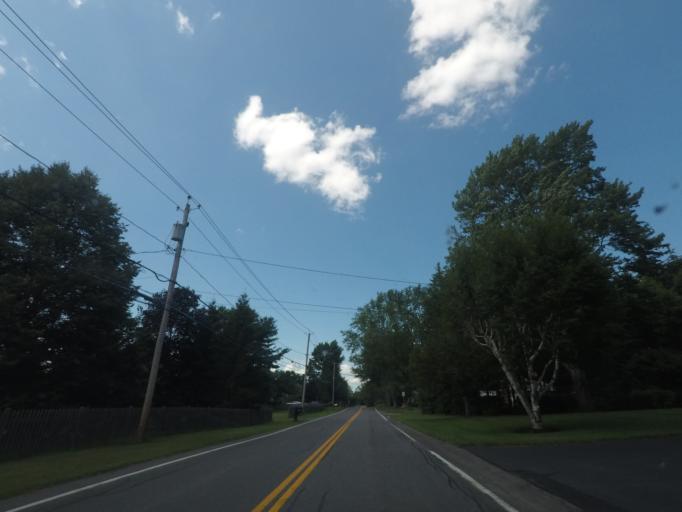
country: US
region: New York
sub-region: Schenectady County
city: Rotterdam
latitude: 42.7618
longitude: -73.9616
